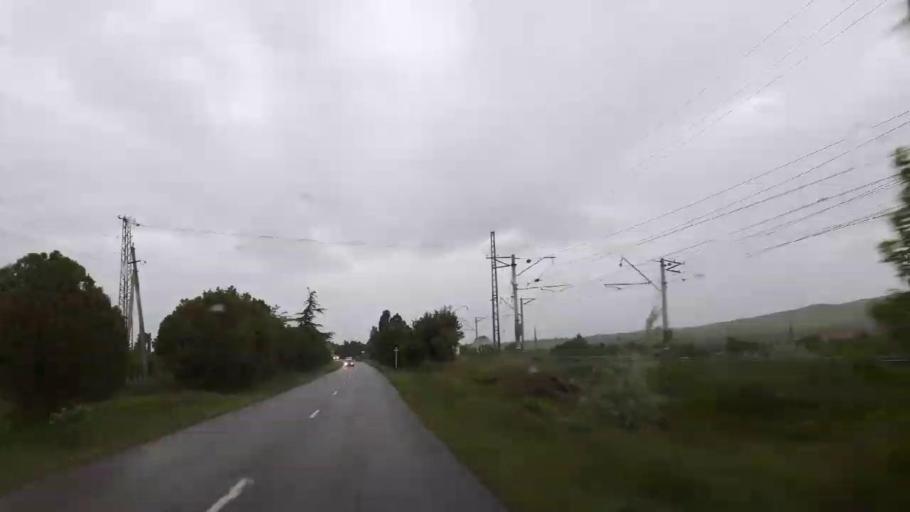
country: GE
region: Shida Kartli
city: Gori
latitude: 41.9968
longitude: 44.0134
